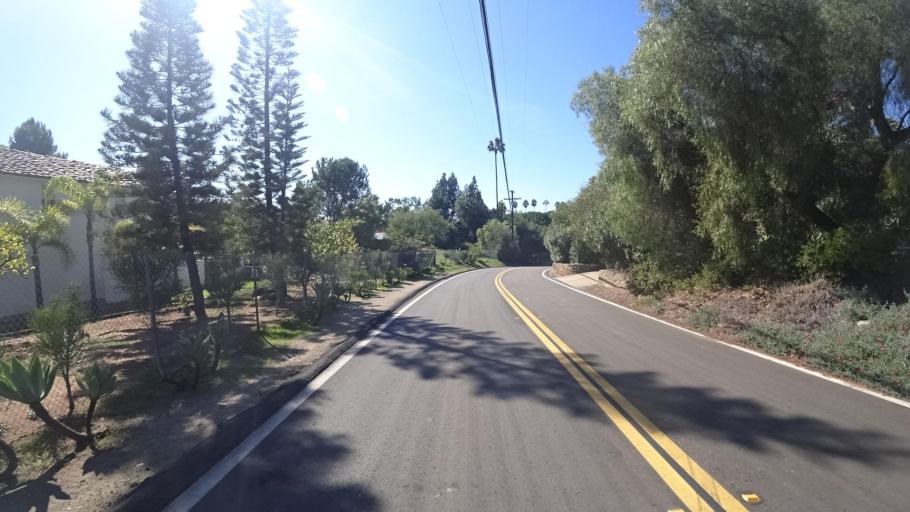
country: US
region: California
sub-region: San Diego County
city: Casa de Oro-Mount Helix
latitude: 32.7639
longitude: -116.9764
